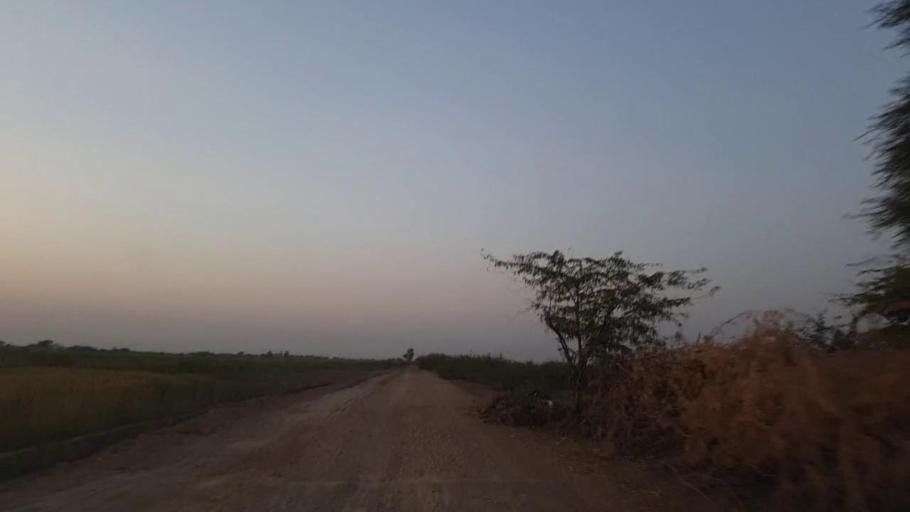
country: PK
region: Sindh
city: Naukot
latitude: 24.8965
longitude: 69.3819
